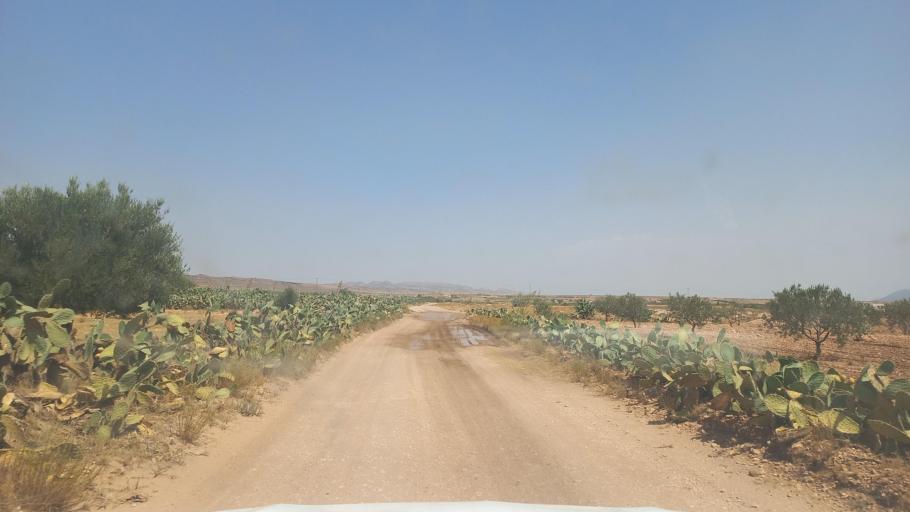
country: TN
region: Al Qasrayn
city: Kasserine
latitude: 35.2820
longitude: 8.9490
